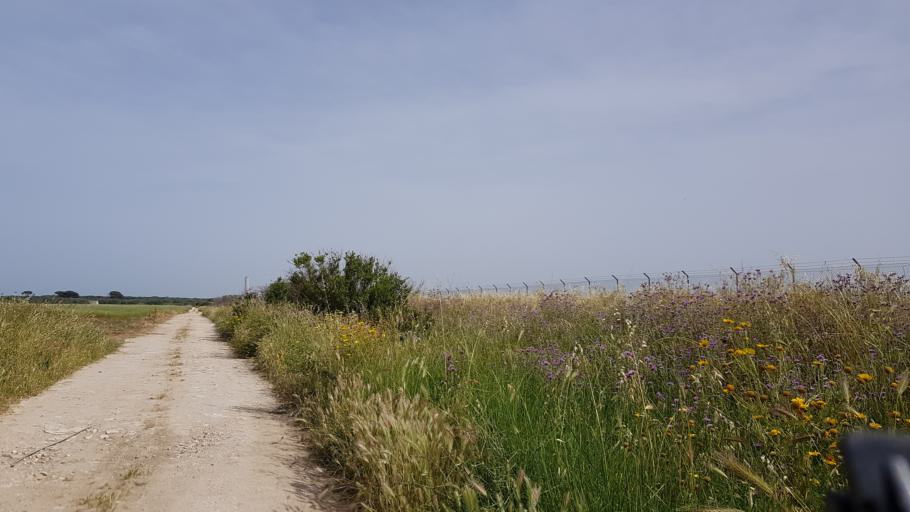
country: IT
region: Apulia
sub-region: Provincia di Brindisi
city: La Rosa
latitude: 40.5944
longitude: 17.9943
